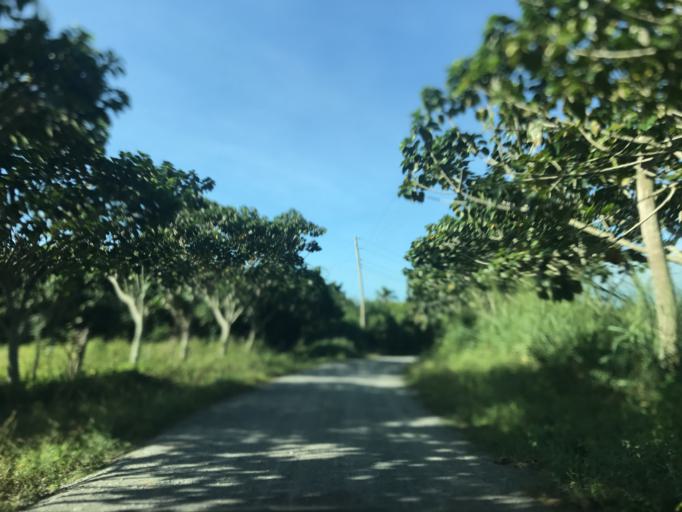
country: CU
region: Camaguey
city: Florida
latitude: 21.4823
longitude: -78.1763
